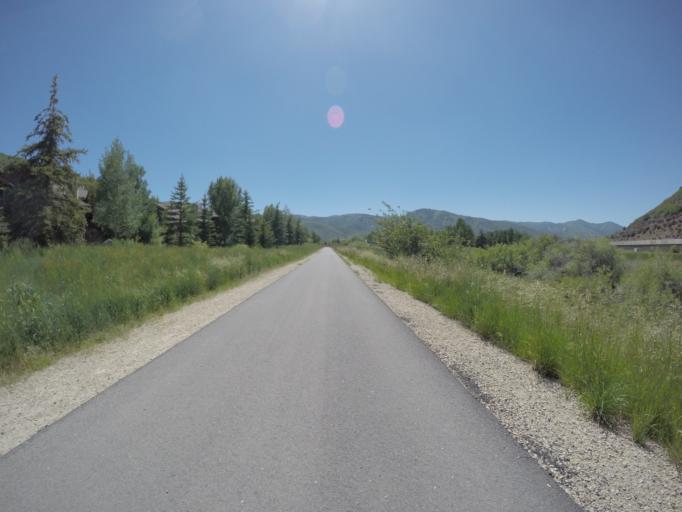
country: US
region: Utah
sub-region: Summit County
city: Park City
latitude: 40.6678
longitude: -111.4825
